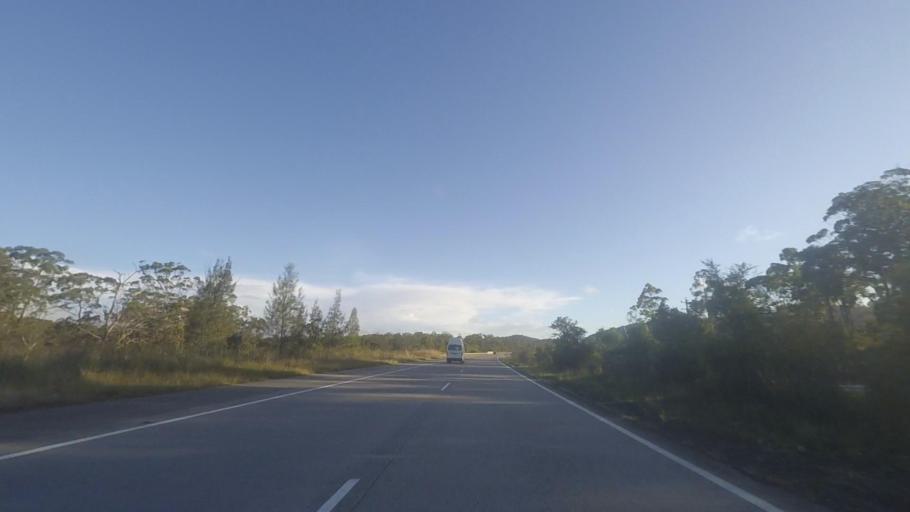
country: AU
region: New South Wales
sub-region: Great Lakes
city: Bulahdelah
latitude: -32.4531
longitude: 152.1978
